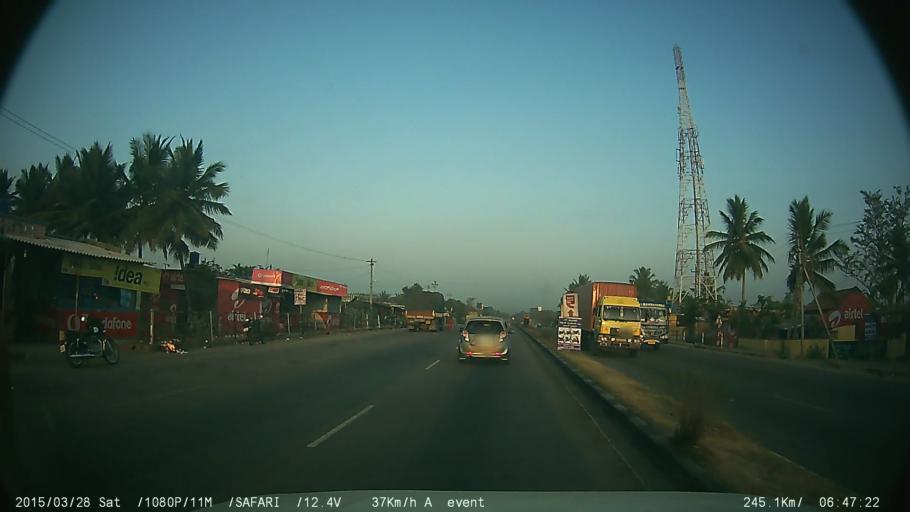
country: IN
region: Karnataka
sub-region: Mandya
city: Maddur
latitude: 12.6132
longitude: 77.0789
